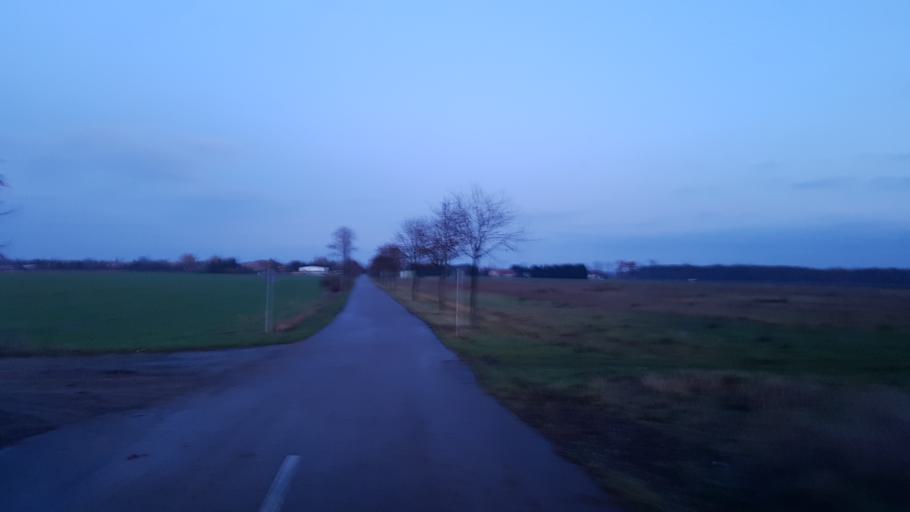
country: DE
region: Brandenburg
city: Falkenberg
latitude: 51.6339
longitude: 13.2244
